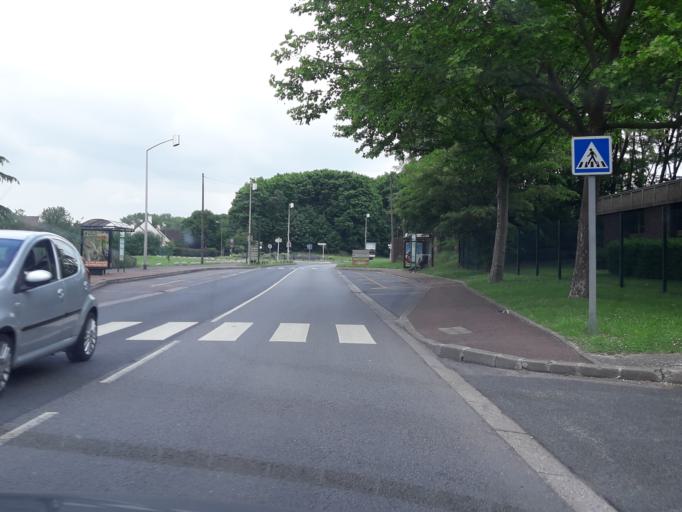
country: FR
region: Ile-de-France
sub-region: Departement de l'Essonne
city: Lisses
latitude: 48.6129
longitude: 2.4221
